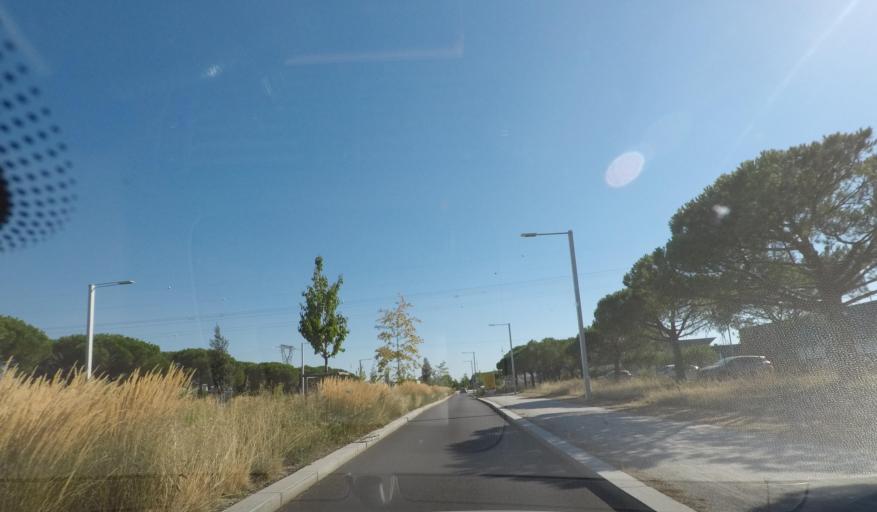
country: FR
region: Pays de la Loire
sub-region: Departement de la Loire-Atlantique
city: Saint-Nazaire
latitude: 47.2950
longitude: -2.2081
